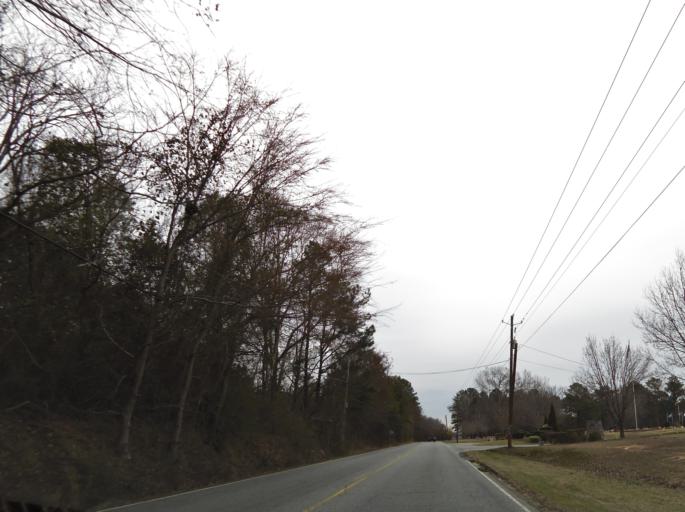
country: US
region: Georgia
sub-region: Houston County
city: Centerville
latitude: 32.7047
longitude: -83.6986
